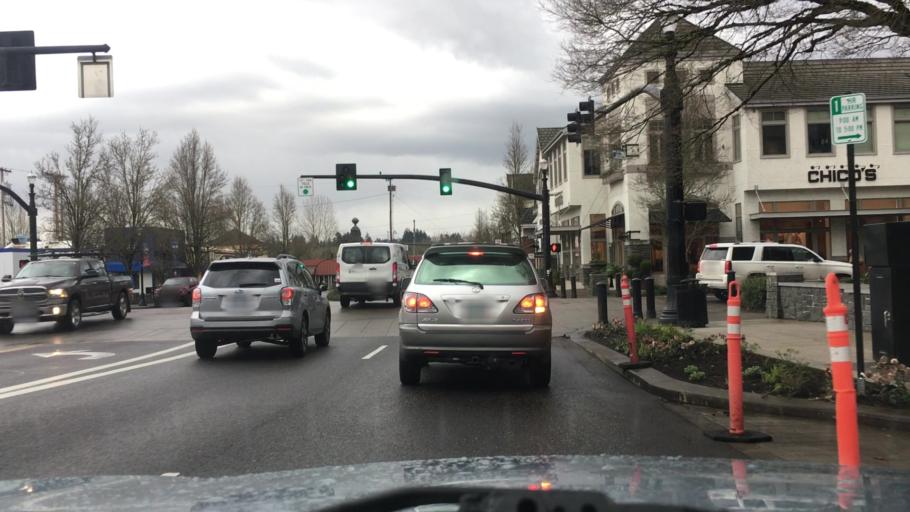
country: US
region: Oregon
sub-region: Clackamas County
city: Lake Oswego
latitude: 45.4194
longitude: -122.6646
